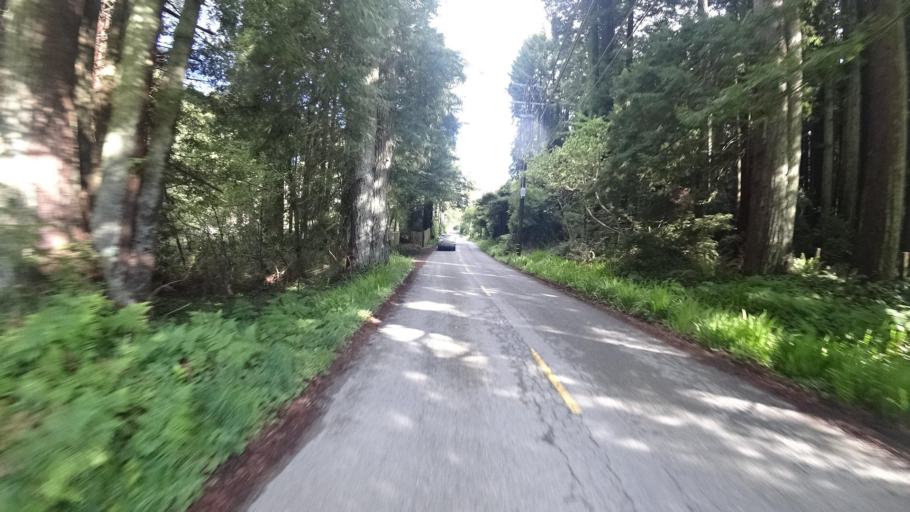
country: US
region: California
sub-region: Humboldt County
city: Westhaven-Moonstone
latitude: 41.0389
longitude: -124.1079
